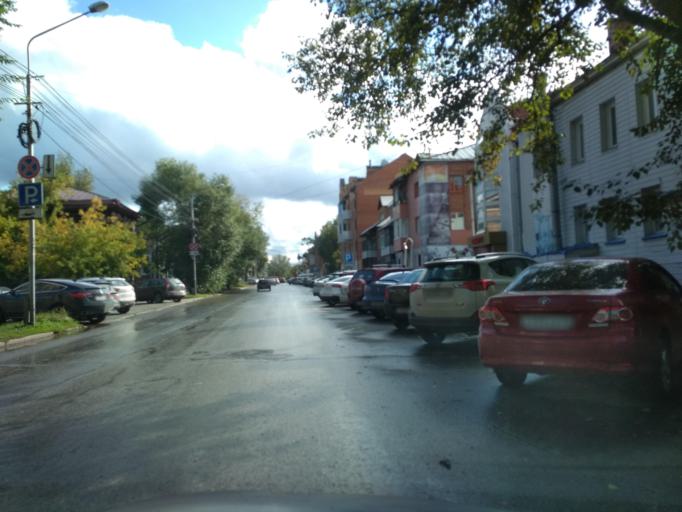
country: RU
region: Tomsk
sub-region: Tomskiy Rayon
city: Tomsk
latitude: 56.4785
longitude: 84.9515
